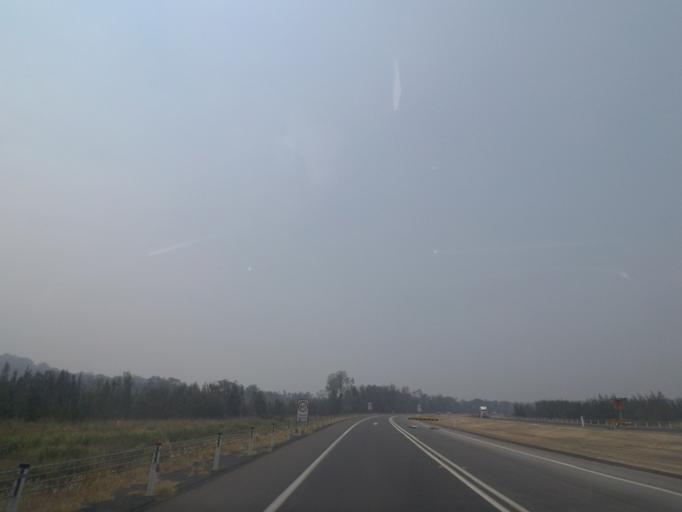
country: AU
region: New South Wales
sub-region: Ballina
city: Ballina
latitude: -28.8709
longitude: 153.4910
